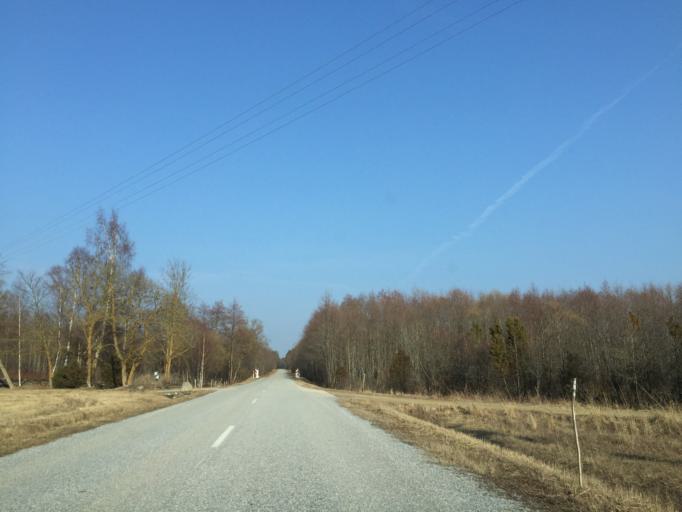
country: EE
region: Saare
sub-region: Orissaare vald
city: Orissaare
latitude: 58.5570
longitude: 23.3225
